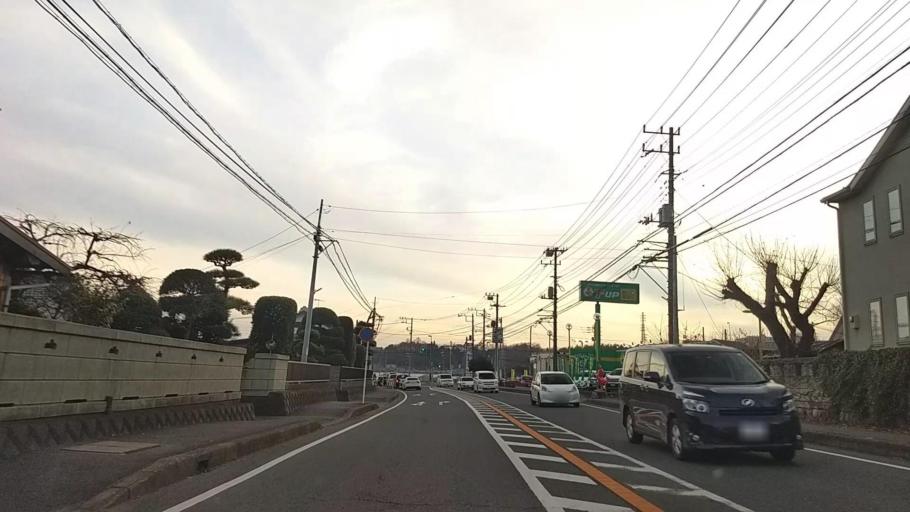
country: JP
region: Kanagawa
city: Atsugi
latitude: 35.4370
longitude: 139.3523
